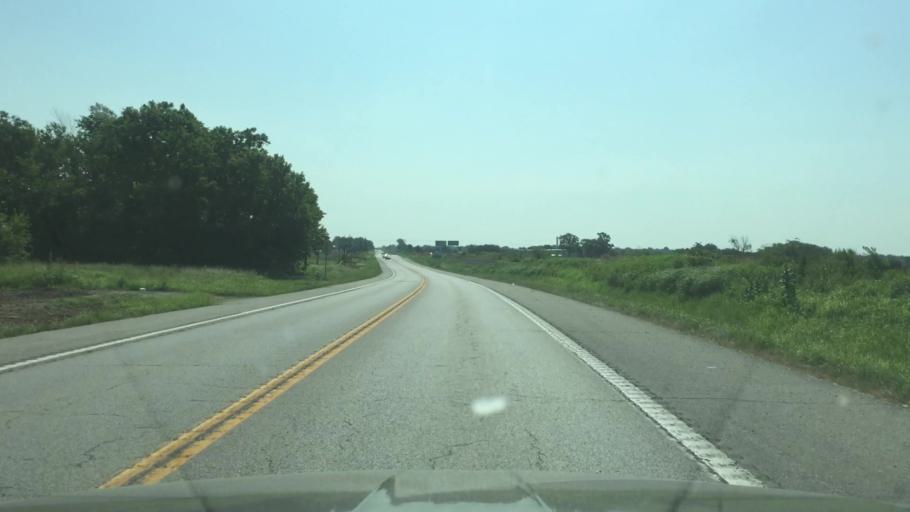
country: US
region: Missouri
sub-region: Pettis County
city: Sedalia
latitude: 38.6966
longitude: -93.1787
